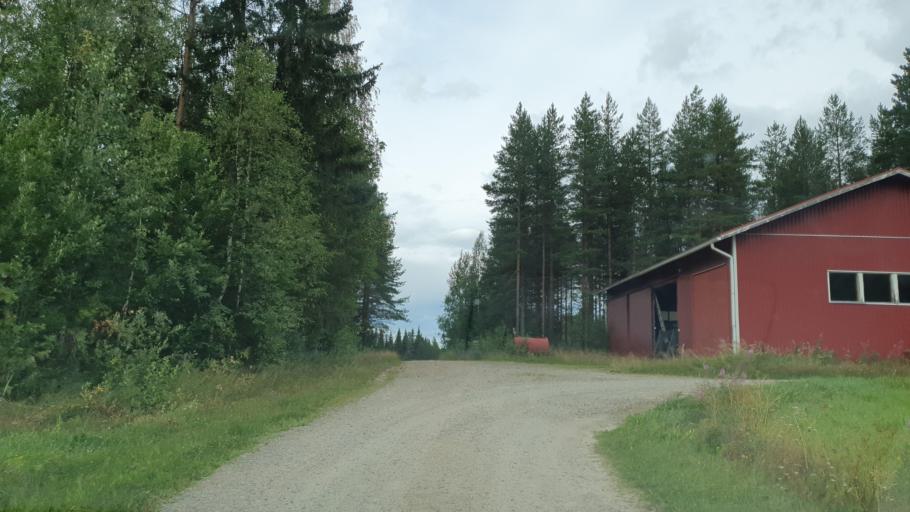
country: FI
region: Kainuu
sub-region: Kehys-Kainuu
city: Kuhmo
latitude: 64.2035
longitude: 29.3792
